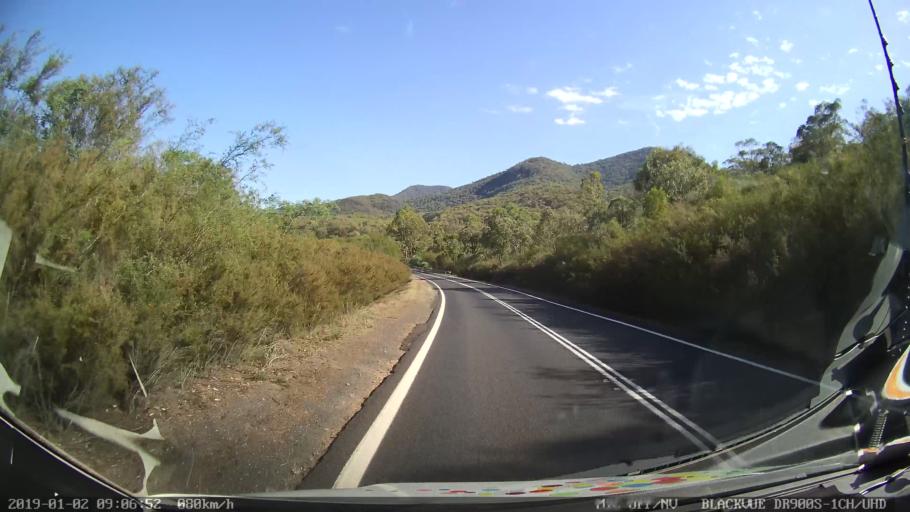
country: AU
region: New South Wales
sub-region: Tumut Shire
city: Tumut
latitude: -35.5462
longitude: 148.3034
